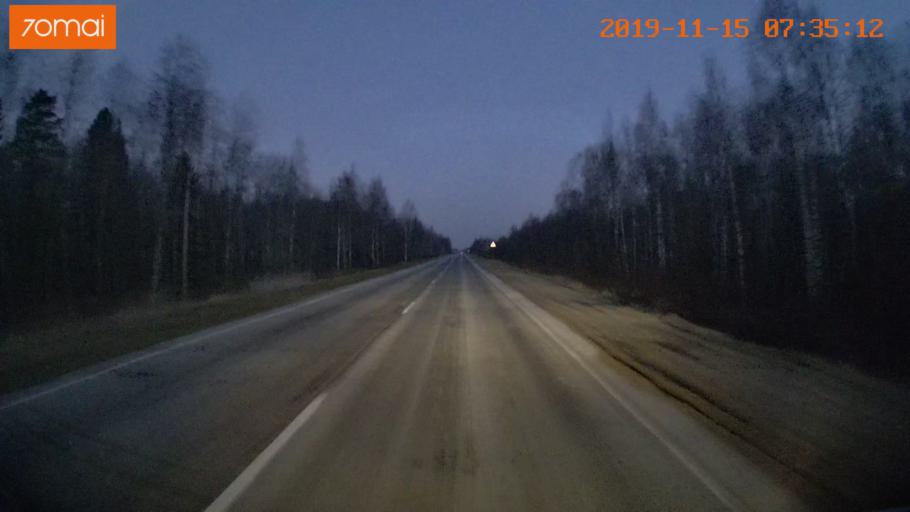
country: RU
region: Vologda
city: Sheksna
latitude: 58.7269
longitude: 38.4575
